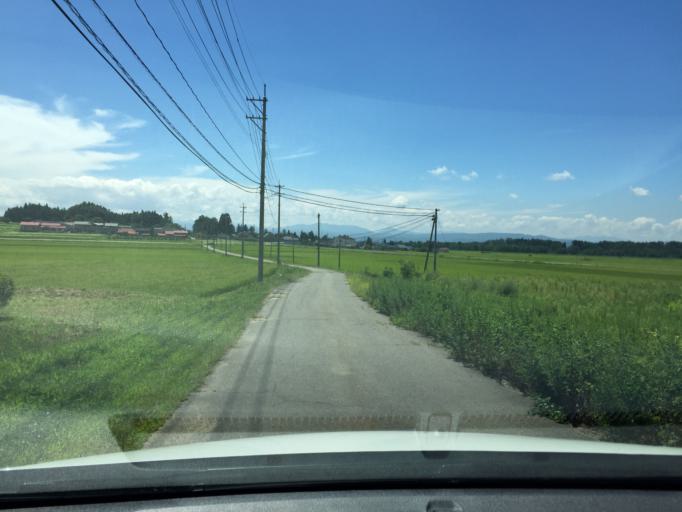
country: JP
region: Fukushima
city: Inawashiro
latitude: 37.5709
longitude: 140.1373
